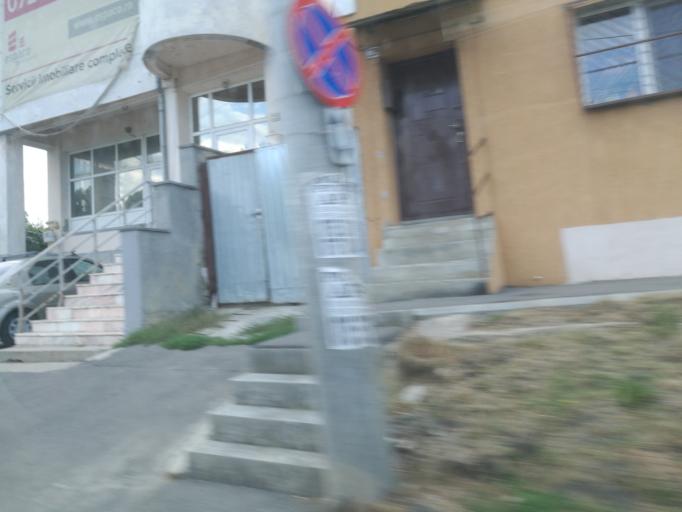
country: RO
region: Ilfov
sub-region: Comuna Mogosoaia
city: Mogosoaia
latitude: 44.5025
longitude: 26.0255
